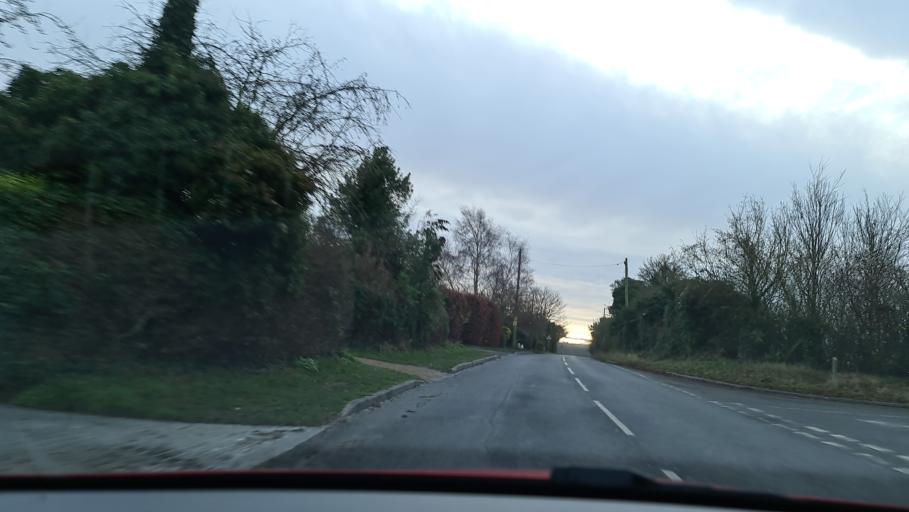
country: GB
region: England
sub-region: Buckinghamshire
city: Princes Risborough
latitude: 51.7207
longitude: -0.8246
